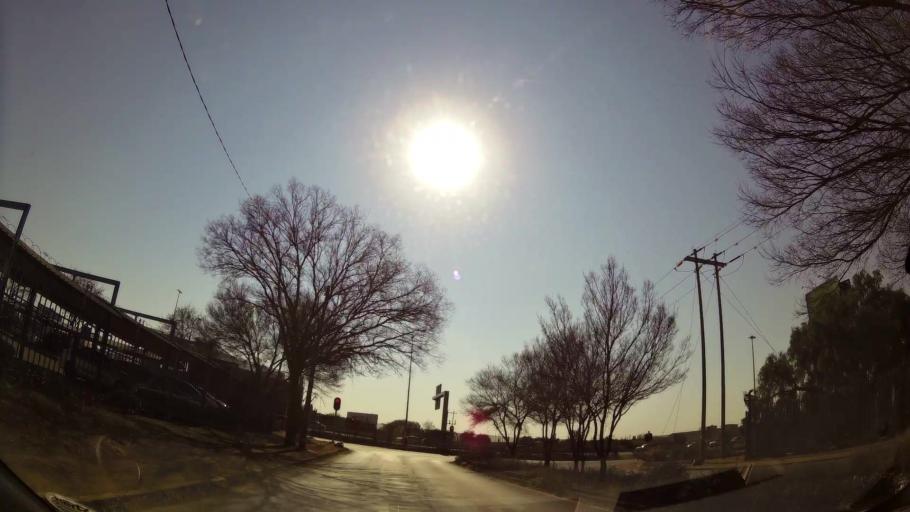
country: ZA
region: Gauteng
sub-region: City of Johannesburg Metropolitan Municipality
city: Modderfontein
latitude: -26.1310
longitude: 28.2173
